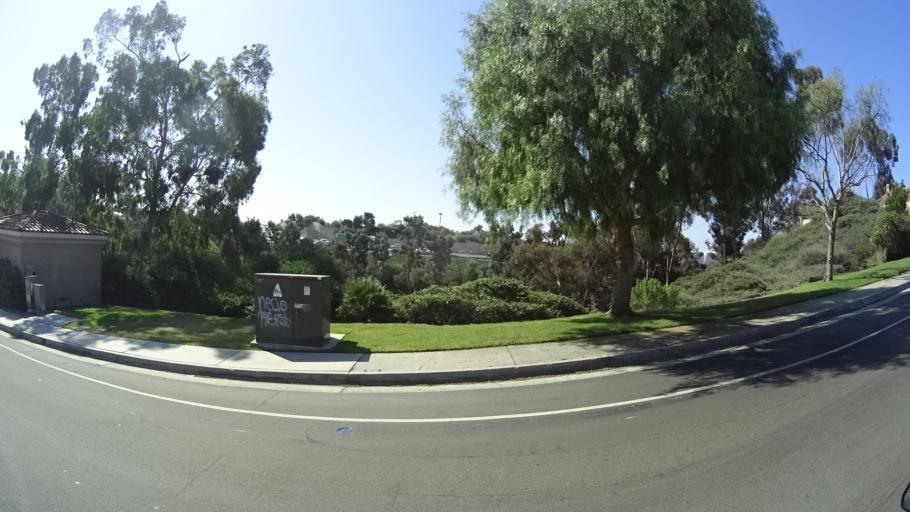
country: US
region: California
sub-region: Orange County
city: San Clemente
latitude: 33.4480
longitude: -117.6334
